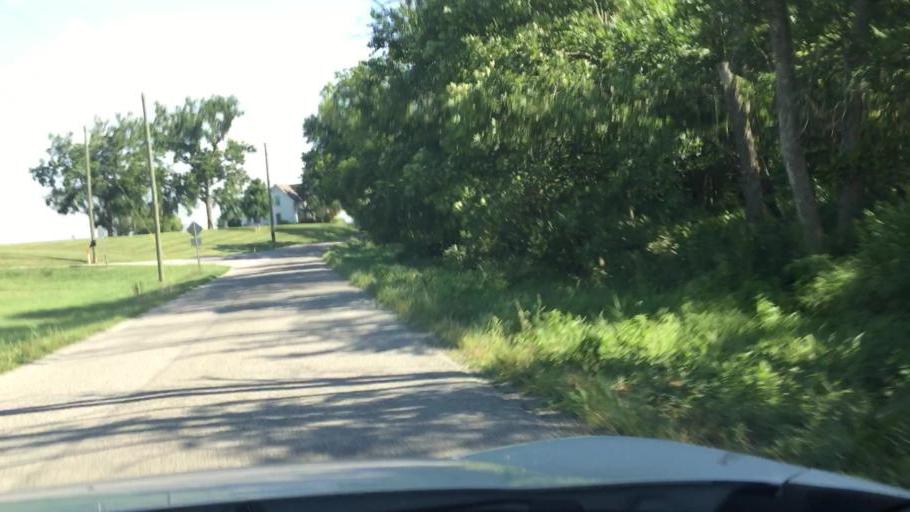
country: US
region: Ohio
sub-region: Champaign County
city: North Lewisburg
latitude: 40.2417
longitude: -83.5211
